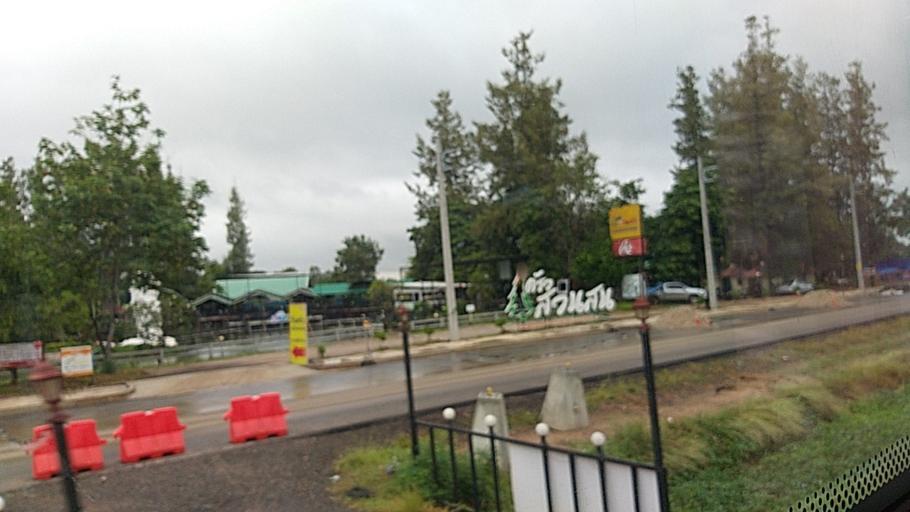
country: TH
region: Nakhon Ratchasima
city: Nakhon Ratchasima
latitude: 14.9936
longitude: 102.0644
